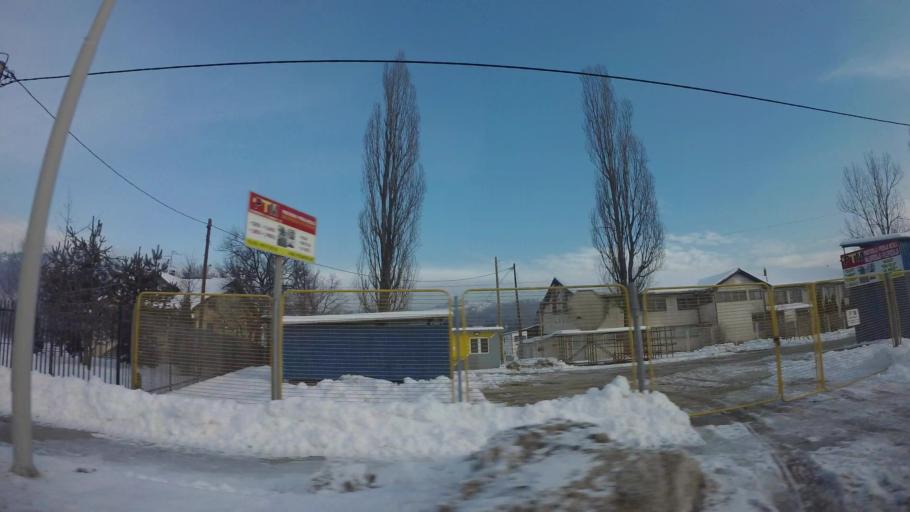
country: BA
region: Federation of Bosnia and Herzegovina
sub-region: Kanton Sarajevo
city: Sarajevo
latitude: 43.8280
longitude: 18.3643
